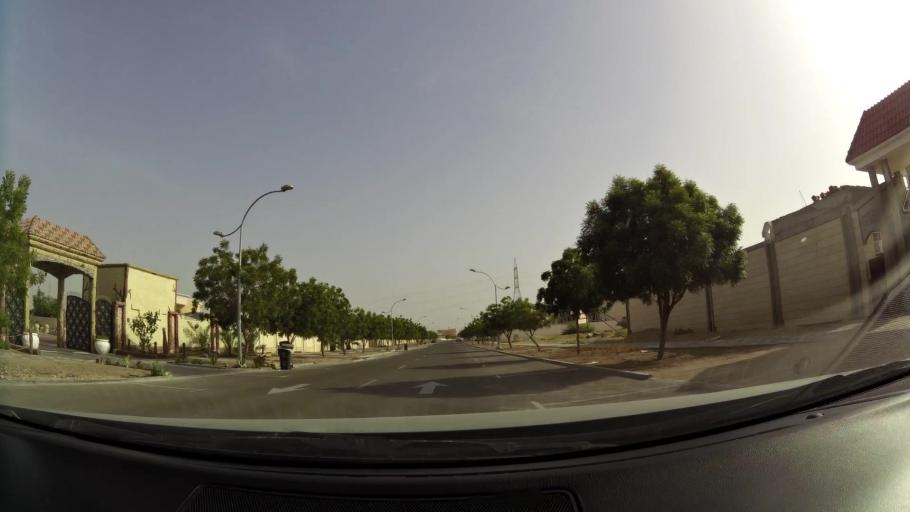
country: AE
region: Abu Dhabi
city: Al Ain
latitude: 24.1438
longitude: 55.7230
